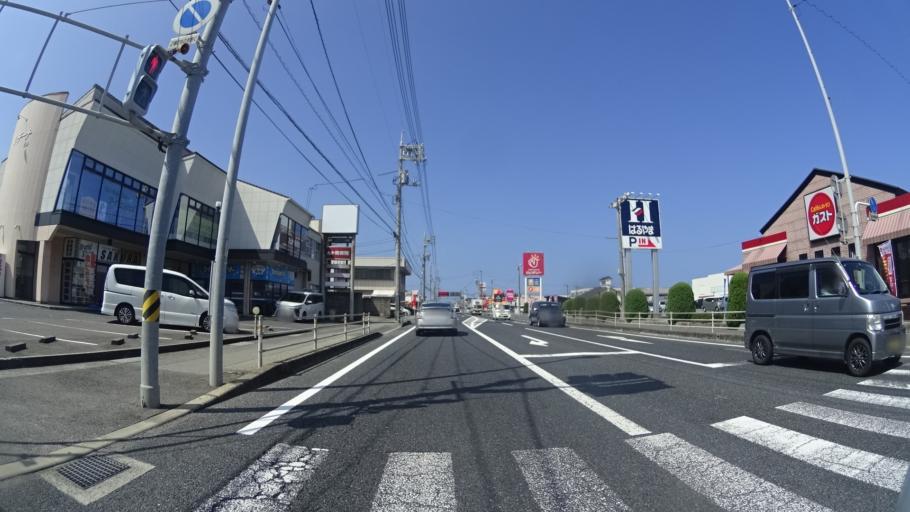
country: JP
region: Shimane
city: Masuda
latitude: 34.6897
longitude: 131.8170
